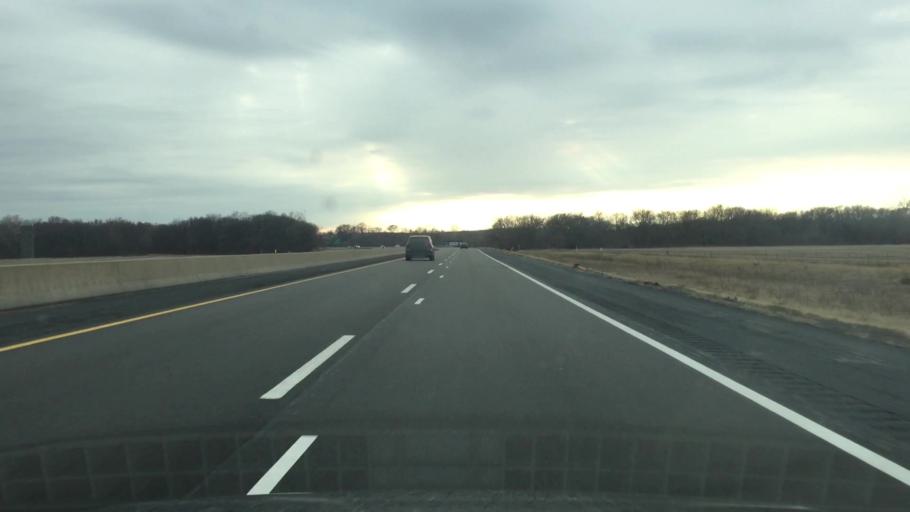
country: US
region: Kansas
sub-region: Osage County
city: Osage City
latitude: 38.6702
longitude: -96.0133
